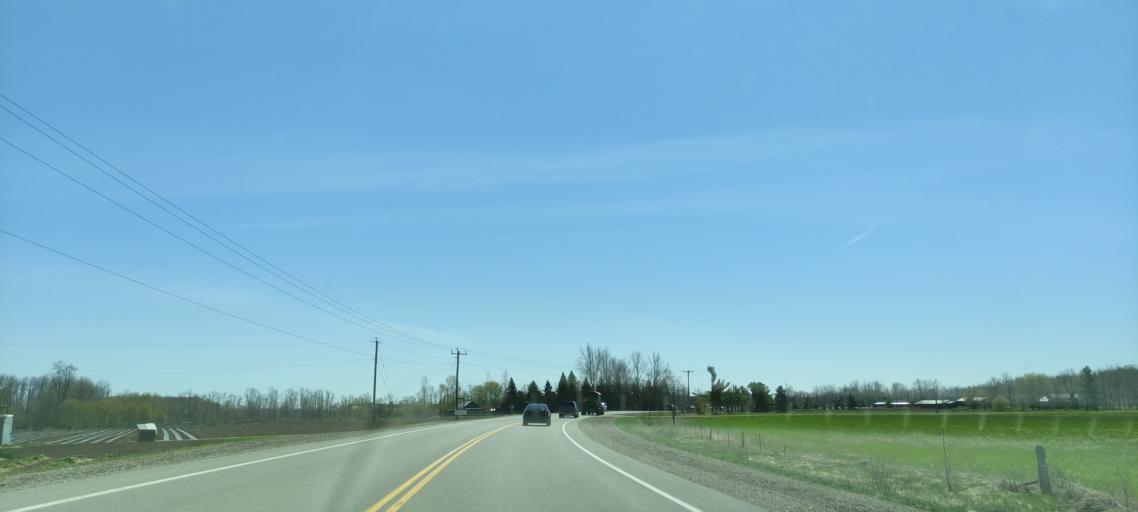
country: CA
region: Ontario
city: Waterloo
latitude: 43.5807
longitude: -80.4167
